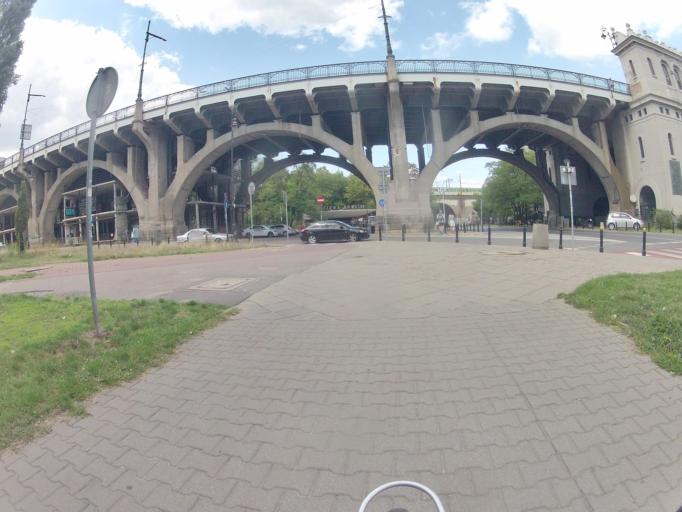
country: PL
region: Masovian Voivodeship
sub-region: Warszawa
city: Srodmiescie
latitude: 52.2333
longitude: 21.0305
